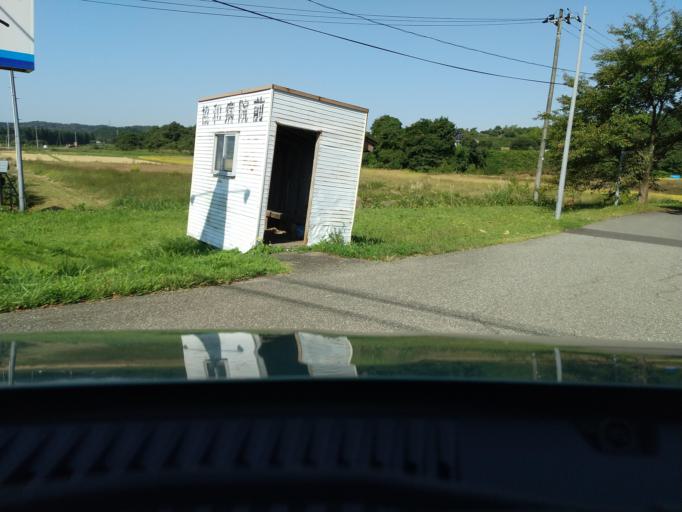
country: JP
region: Akita
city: Akita
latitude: 39.5953
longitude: 140.3015
